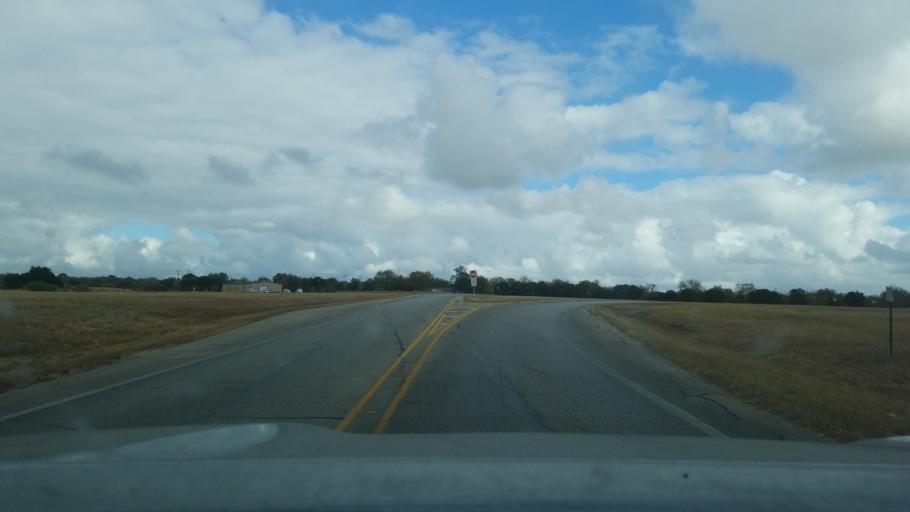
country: US
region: Texas
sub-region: Bexar County
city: Universal City
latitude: 29.5396
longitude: -98.2977
